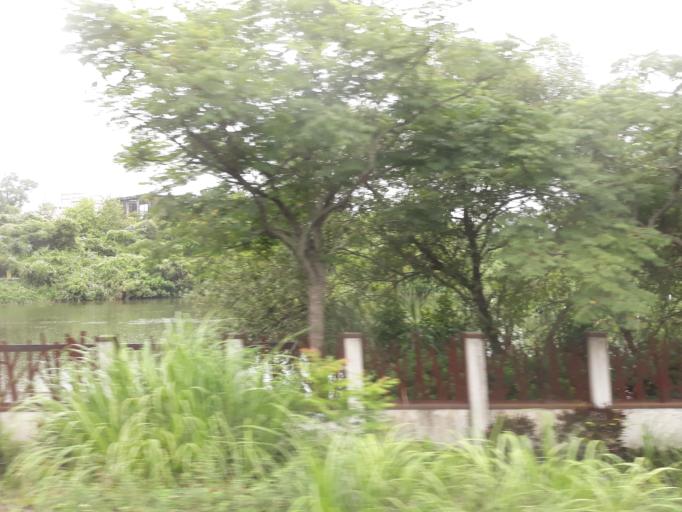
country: TW
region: Taiwan
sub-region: Yilan
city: Yilan
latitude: 24.6819
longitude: 121.7746
